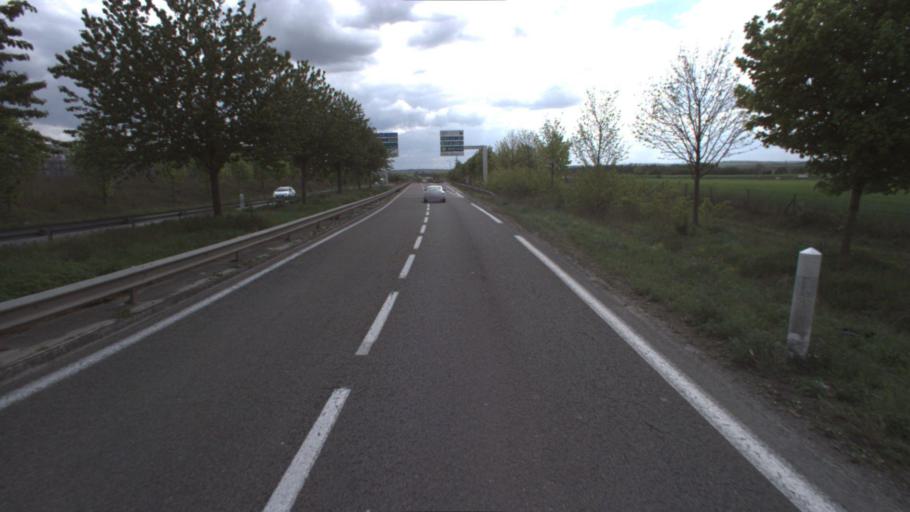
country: FR
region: Ile-de-France
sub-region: Departement de Seine-et-Marne
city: Chauconin-Neufmontiers
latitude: 48.9609
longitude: 2.8587
